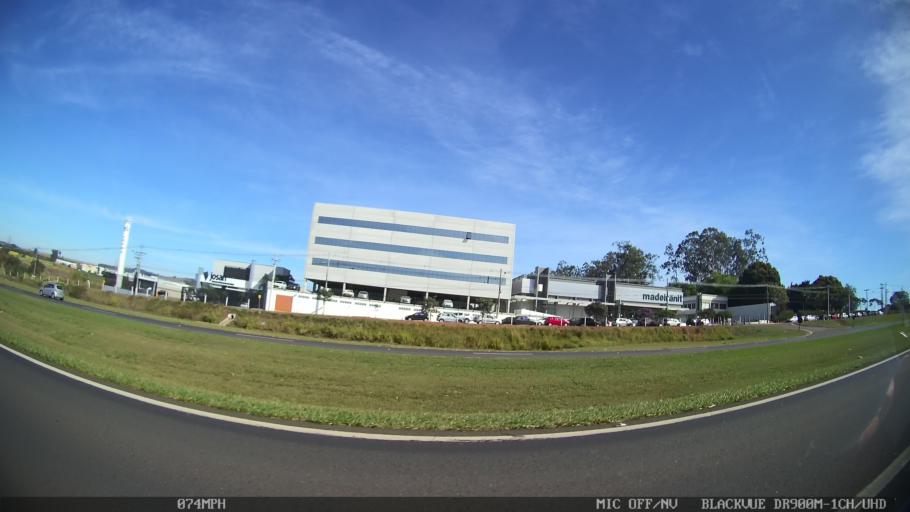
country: BR
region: Sao Paulo
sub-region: Leme
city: Leme
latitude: -22.2068
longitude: -47.3948
